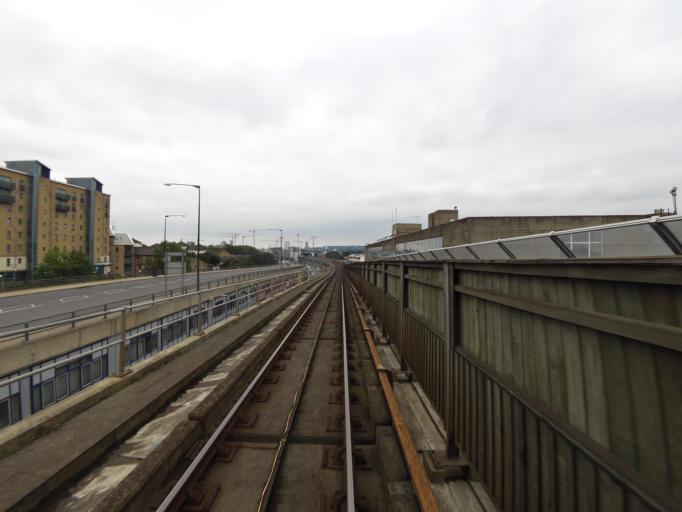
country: GB
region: England
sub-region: Greater London
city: Poplar
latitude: 51.5054
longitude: 0.0163
